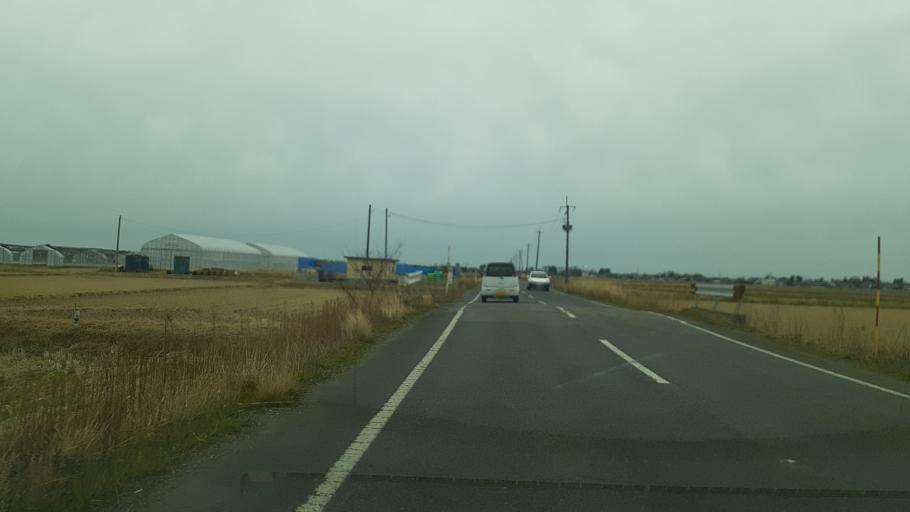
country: JP
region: Niigata
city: Niitsu-honcho
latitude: 37.8254
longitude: 139.0840
